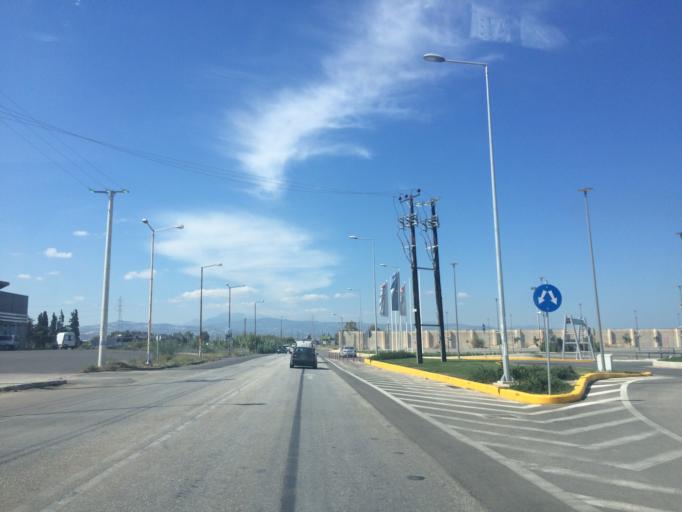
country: GR
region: Peloponnese
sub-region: Nomos Korinthias
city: Arkhaia Korinthos
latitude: 37.9308
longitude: 22.8737
